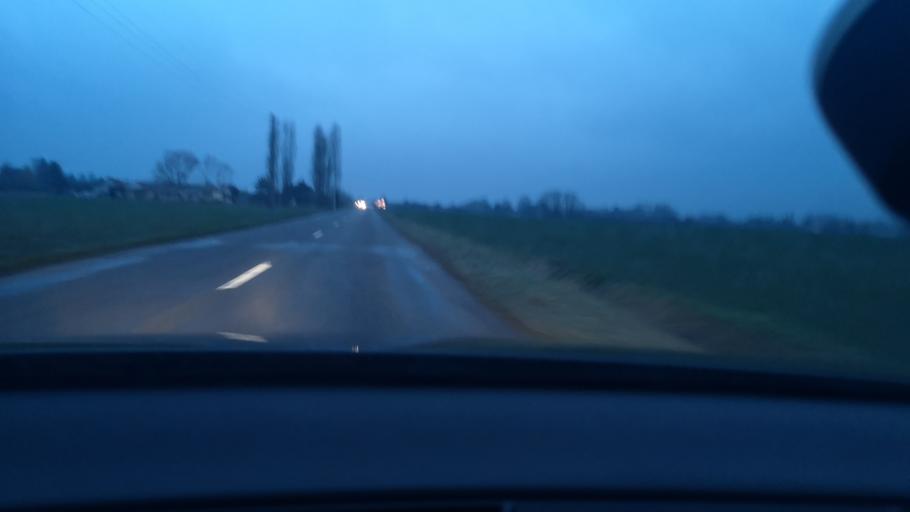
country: FR
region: Bourgogne
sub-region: Departement de Saone-et-Loire
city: Demigny
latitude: 46.9340
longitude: 4.8518
